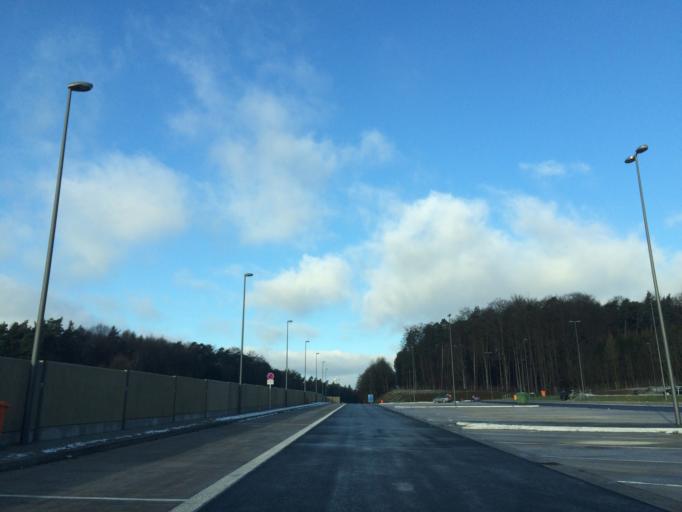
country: DE
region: Hesse
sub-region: Regierungsbezirk Kassel
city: Burghaun
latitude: 50.7138
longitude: 9.6608
